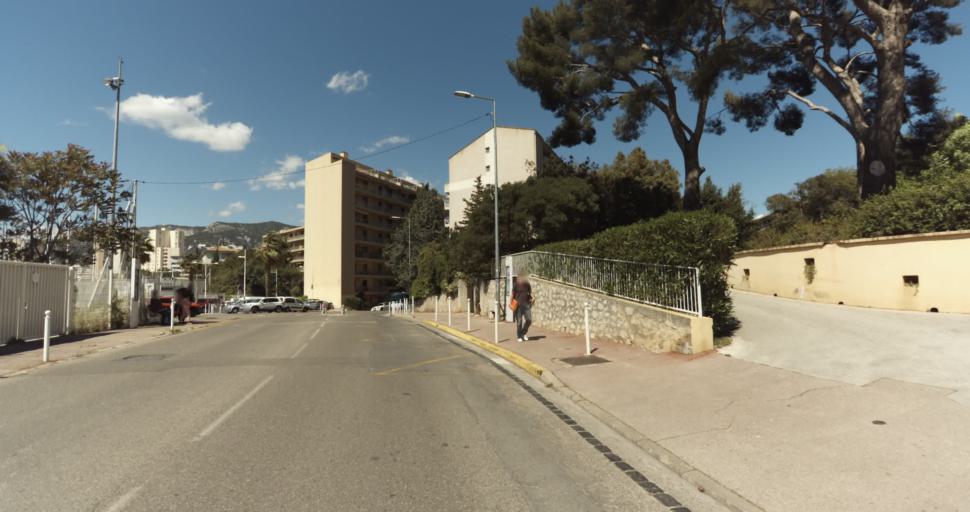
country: FR
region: Provence-Alpes-Cote d'Azur
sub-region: Departement du Var
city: Toulon
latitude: 43.1155
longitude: 5.9454
